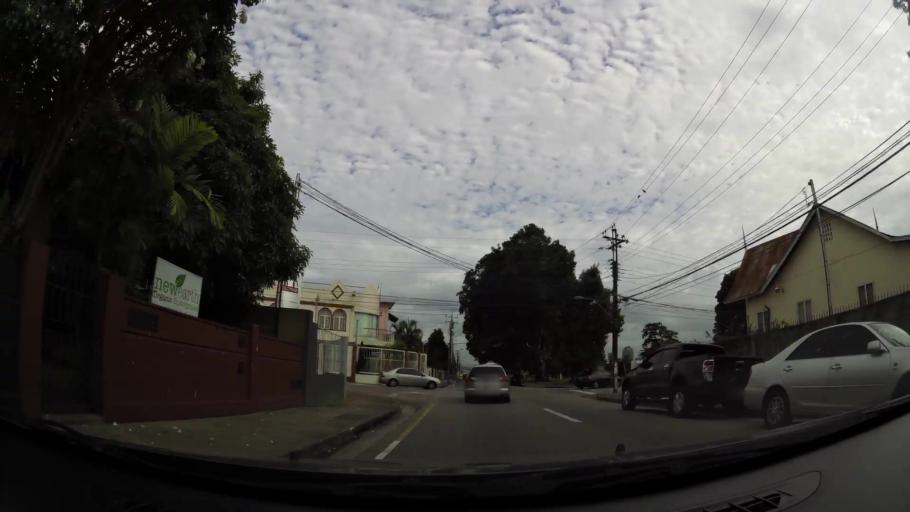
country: TT
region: City of Port of Spain
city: Port-of-Spain
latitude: 10.6636
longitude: -61.5218
